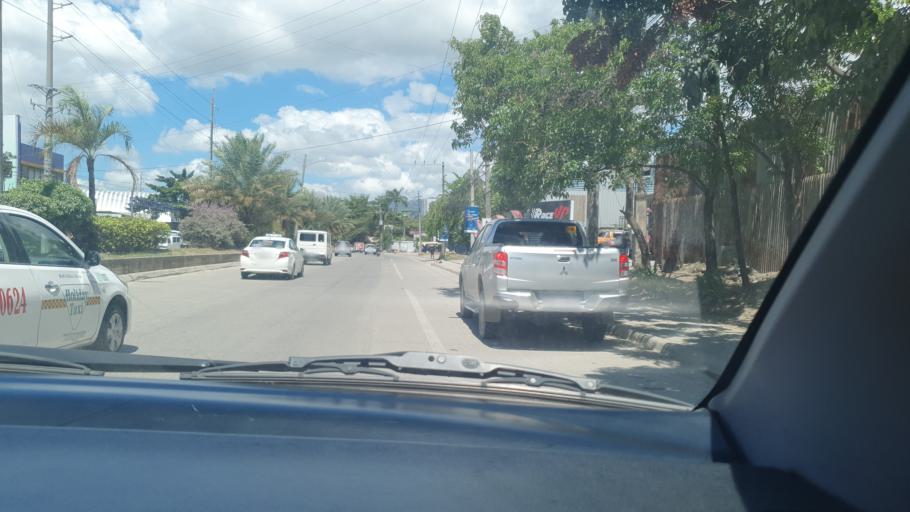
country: PH
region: Central Visayas
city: Mandaue City
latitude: 10.3204
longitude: 123.9285
